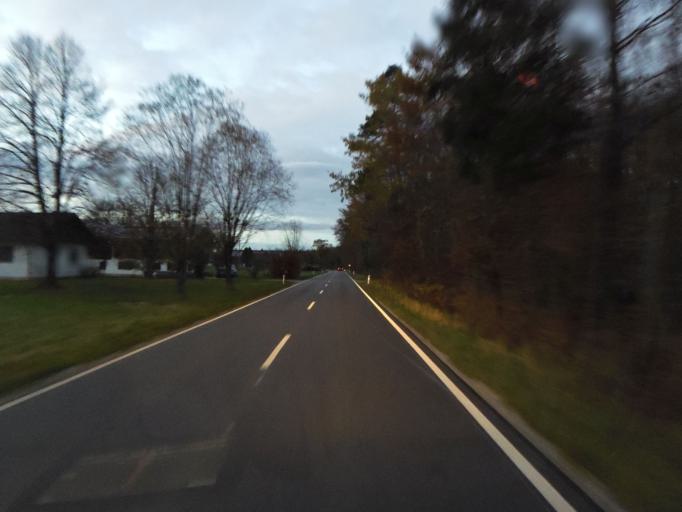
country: DE
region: Bavaria
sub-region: Upper Bavaria
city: Aying
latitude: 47.9314
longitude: 11.7571
